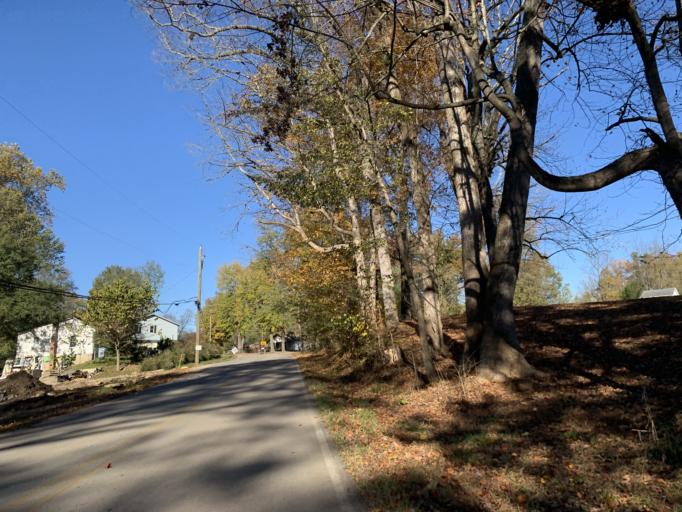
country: US
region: Kentucky
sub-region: Jefferson County
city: Pleasure Ridge Park
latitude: 38.1502
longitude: -85.8779
